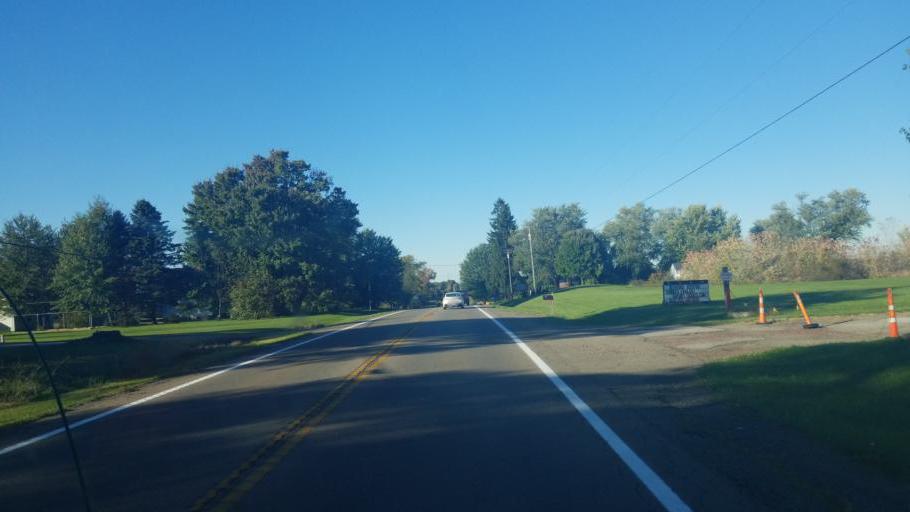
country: US
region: Ohio
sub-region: Columbiana County
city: New Waterford
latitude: 40.8513
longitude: -80.6508
